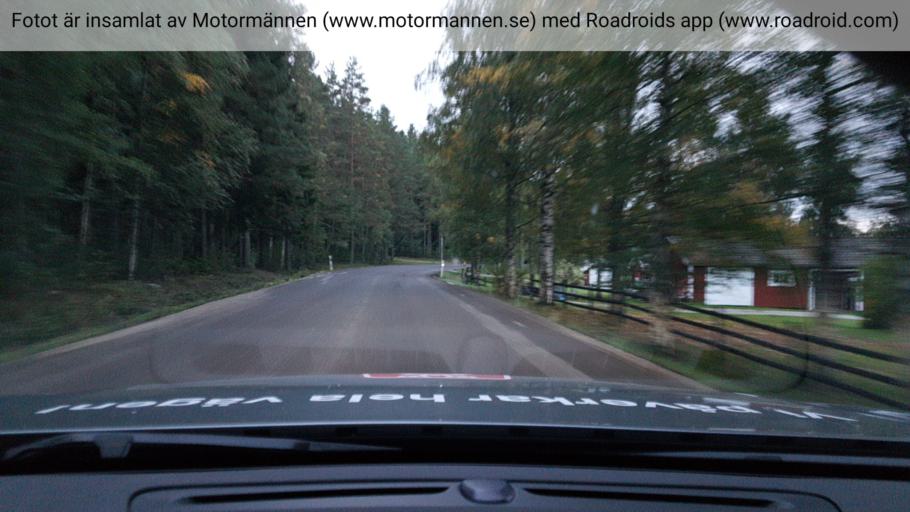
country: SE
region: OErebro
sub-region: Nora Kommun
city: As
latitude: 59.4775
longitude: 14.9168
